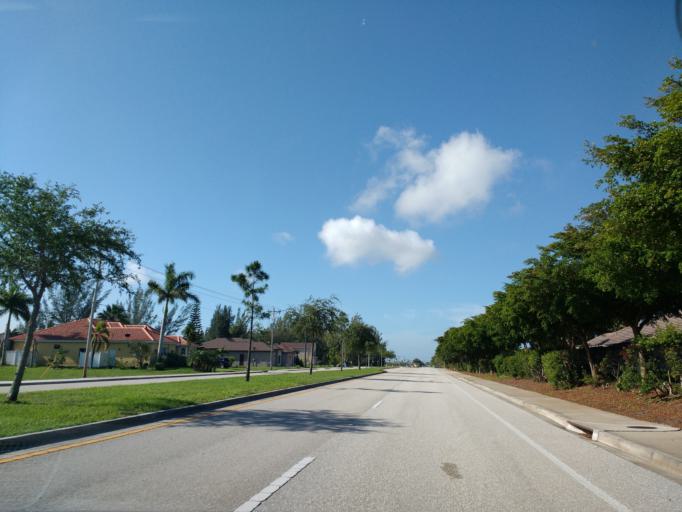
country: US
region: Florida
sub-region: Lee County
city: Cape Coral
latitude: 26.6127
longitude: -82.0235
